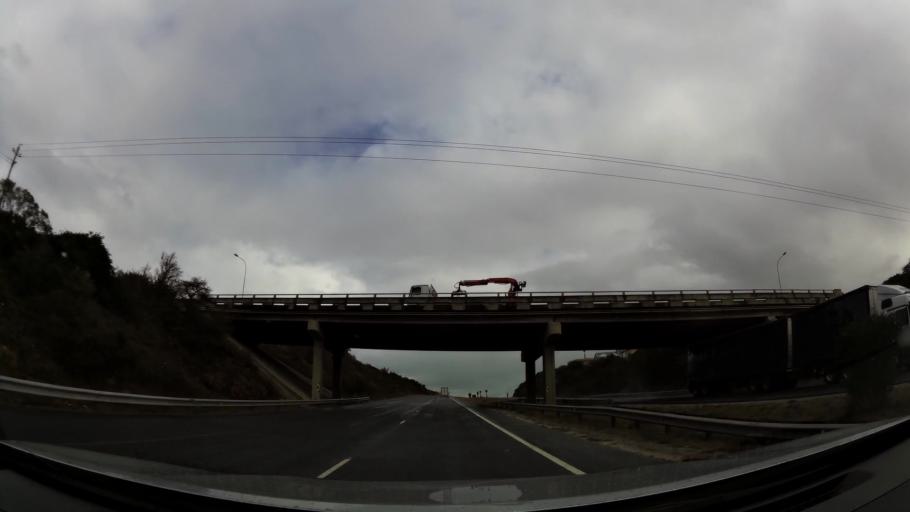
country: ZA
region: Western Cape
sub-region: Eden District Municipality
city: Mossel Bay
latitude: -34.1209
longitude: 22.1061
